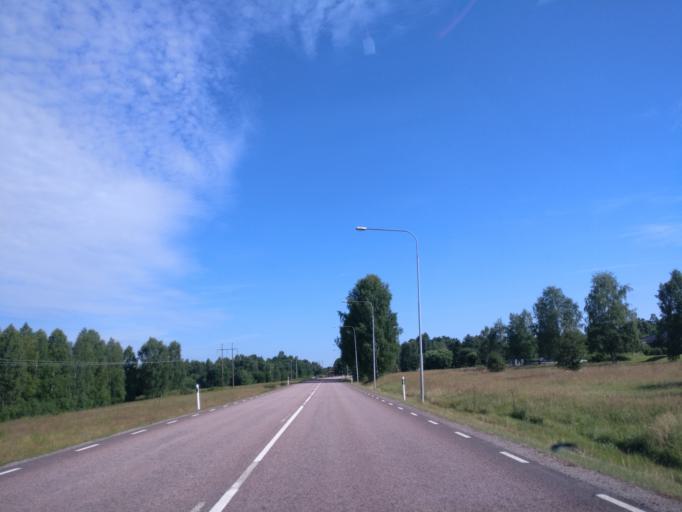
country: SE
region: Vaermland
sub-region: Hagfors Kommun
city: Hagfors
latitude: 60.0517
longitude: 13.7044
